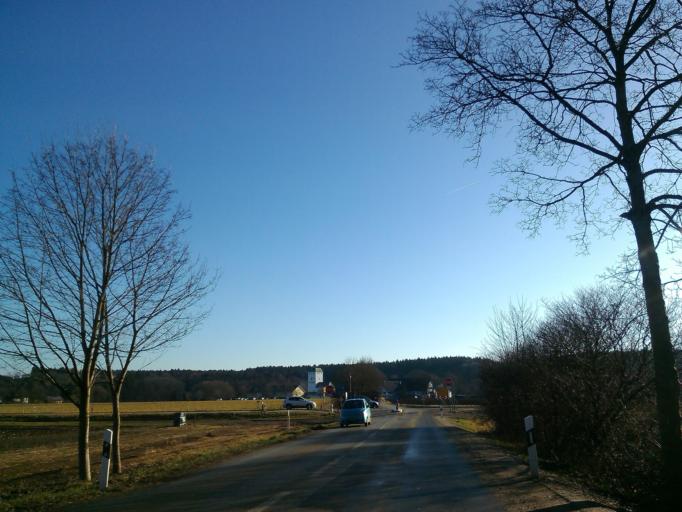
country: DE
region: Bavaria
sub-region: Upper Bavaria
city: Gauting
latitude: 48.0572
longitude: 11.3686
